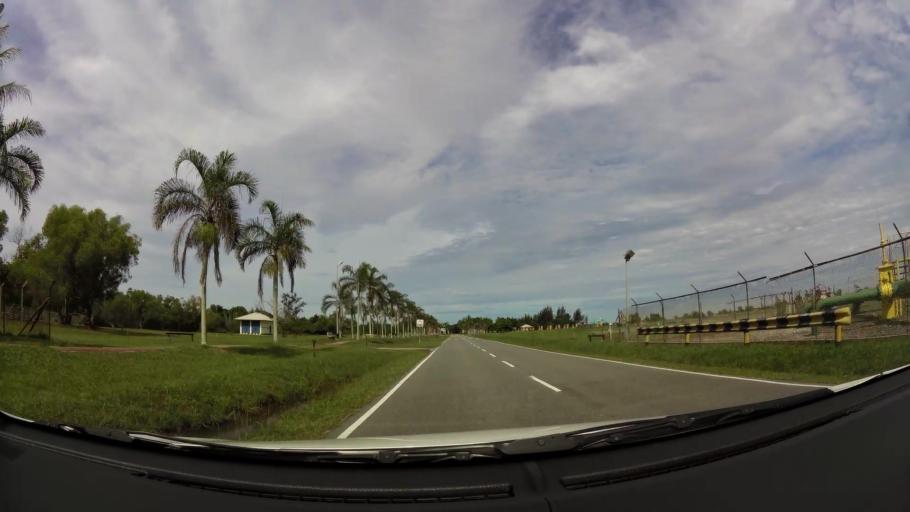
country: BN
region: Belait
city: Seria
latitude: 4.6166
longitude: 114.3206
